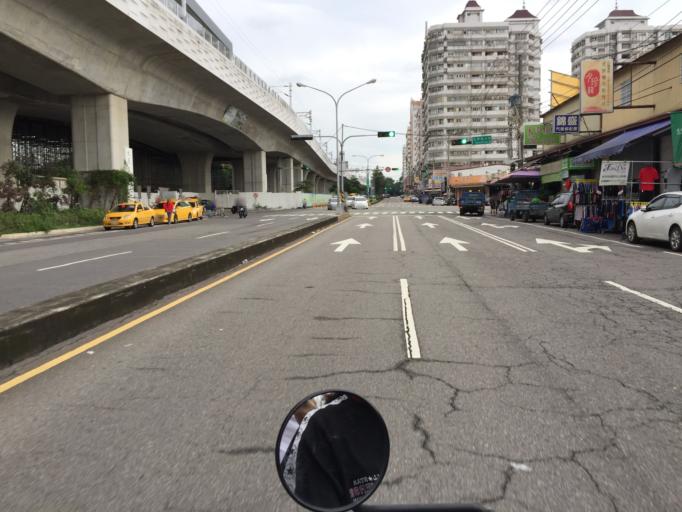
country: TW
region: Taiwan
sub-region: Taichung City
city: Taichung
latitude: 24.1642
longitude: 120.7001
